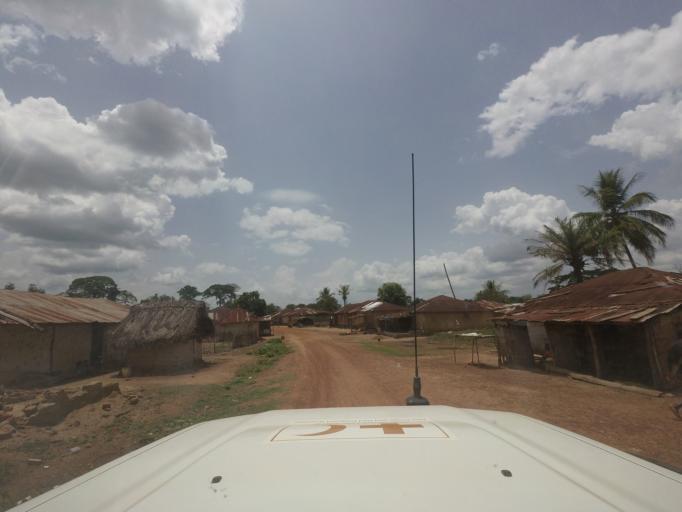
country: LR
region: Bong
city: Gbarnga
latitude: 7.1279
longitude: -9.2288
